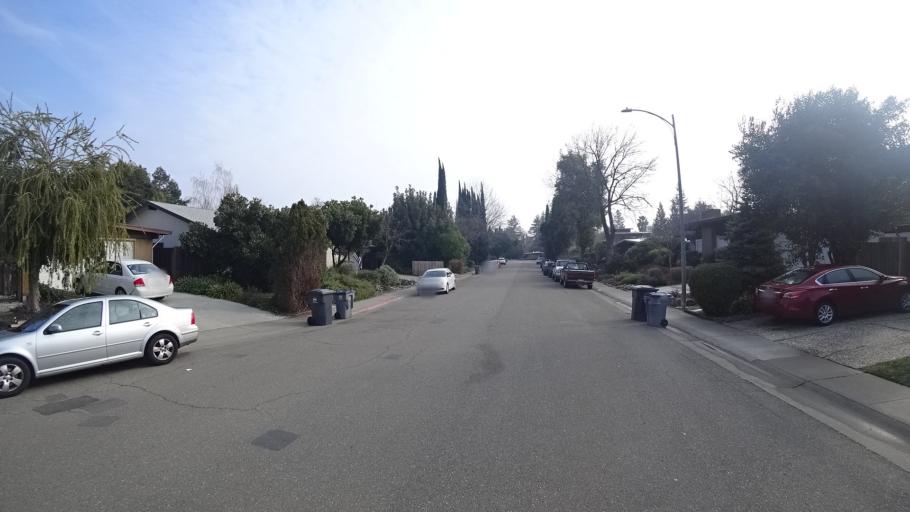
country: US
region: California
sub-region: Yolo County
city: Davis
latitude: 38.5572
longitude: -121.7667
